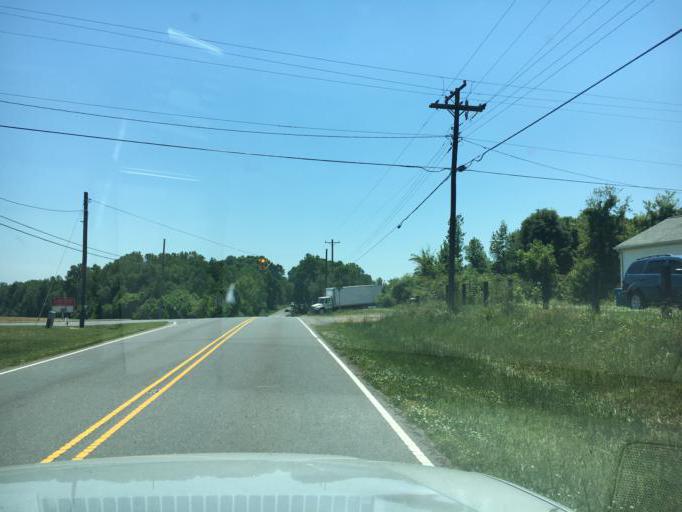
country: US
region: North Carolina
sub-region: Cleveland County
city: Shelby
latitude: 35.2039
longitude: -81.5628
